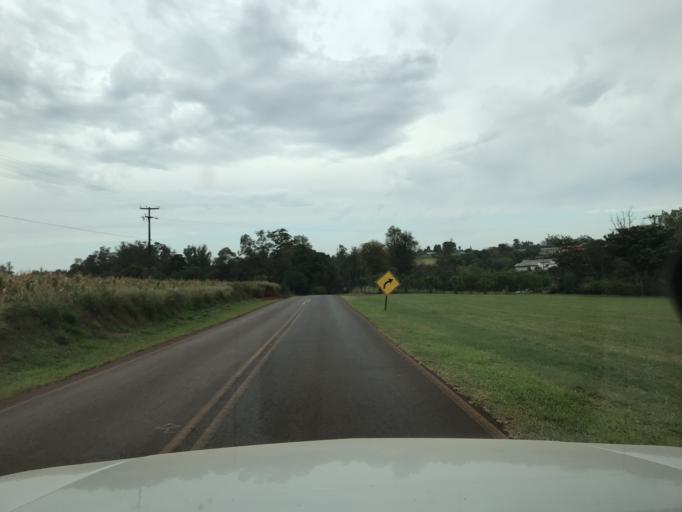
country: BR
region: Parana
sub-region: Marechal Candido Rondon
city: Marechal Candido Rondon
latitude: -24.4542
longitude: -53.9334
